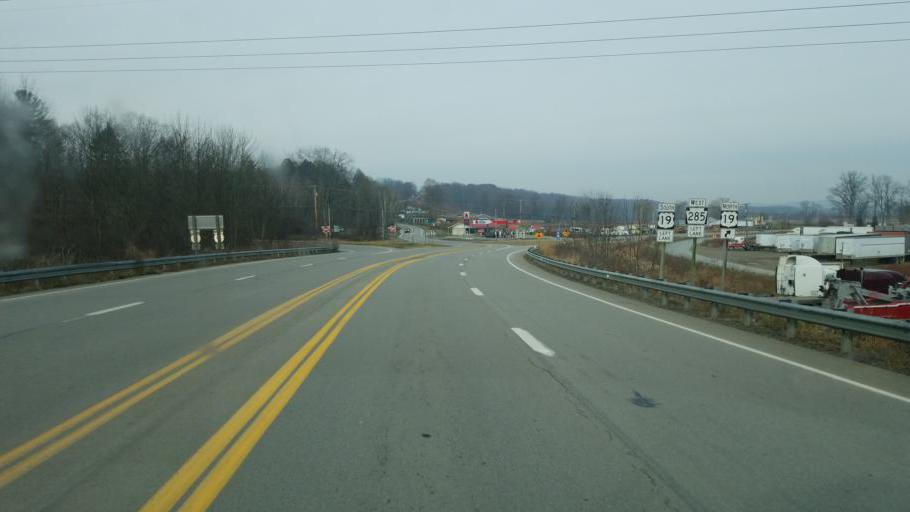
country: US
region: Pennsylvania
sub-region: Crawford County
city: Meadville
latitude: 41.5403
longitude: -80.1854
